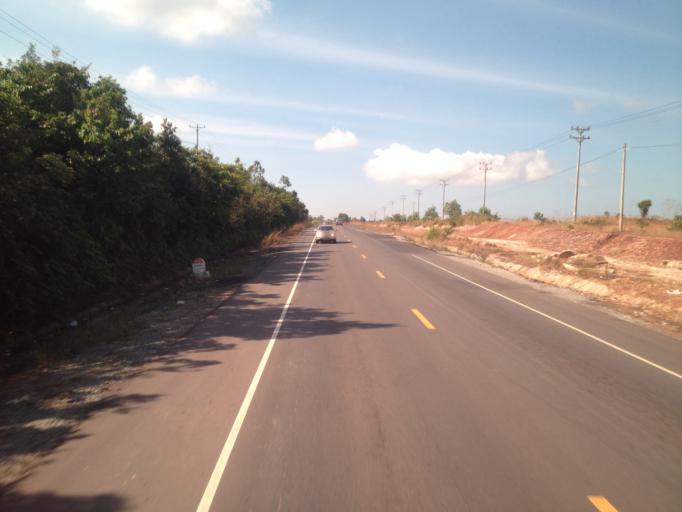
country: KH
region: Preah Sihanouk
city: Sihanoukville
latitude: 10.6035
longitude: 103.6104
